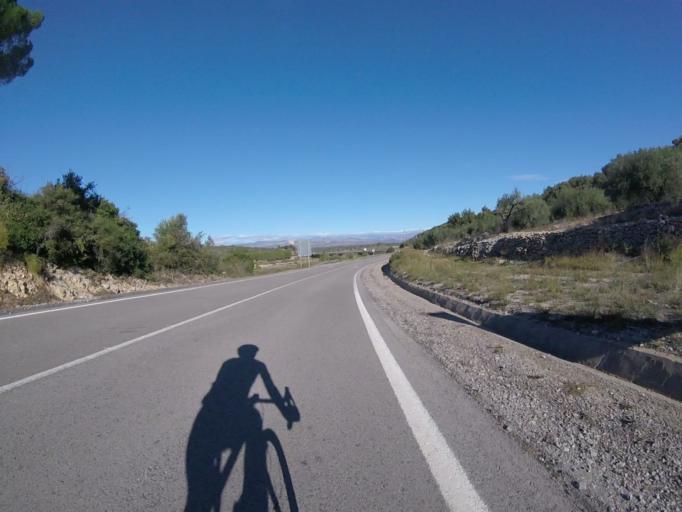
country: ES
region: Valencia
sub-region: Provincia de Castello
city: Cervera del Maestre
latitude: 40.4633
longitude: 0.2519
